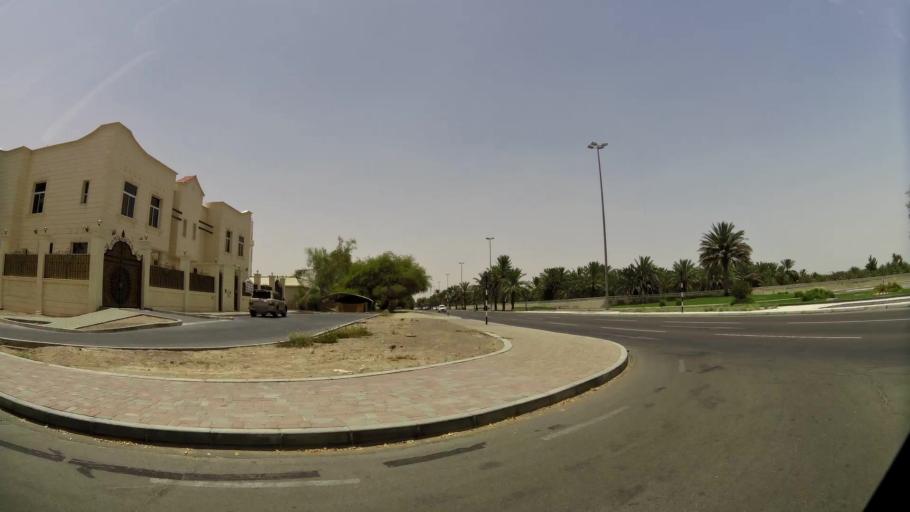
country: AE
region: Abu Dhabi
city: Al Ain
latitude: 24.2157
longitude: 55.7239
